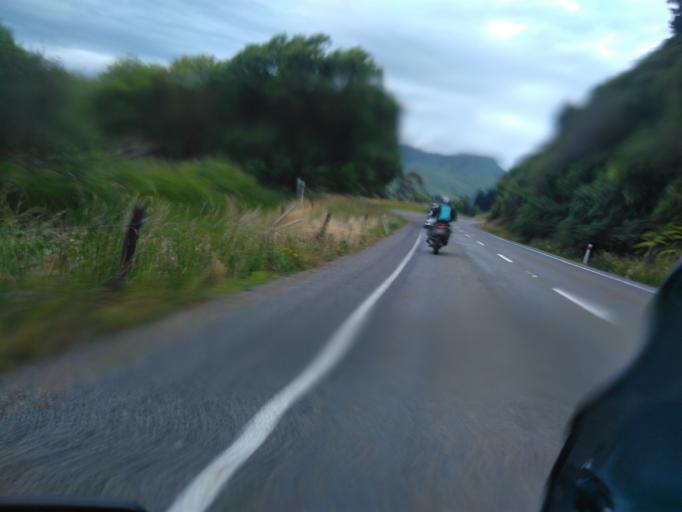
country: NZ
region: Bay of Plenty
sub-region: Opotiki District
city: Opotiki
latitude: -38.3647
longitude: 177.5145
